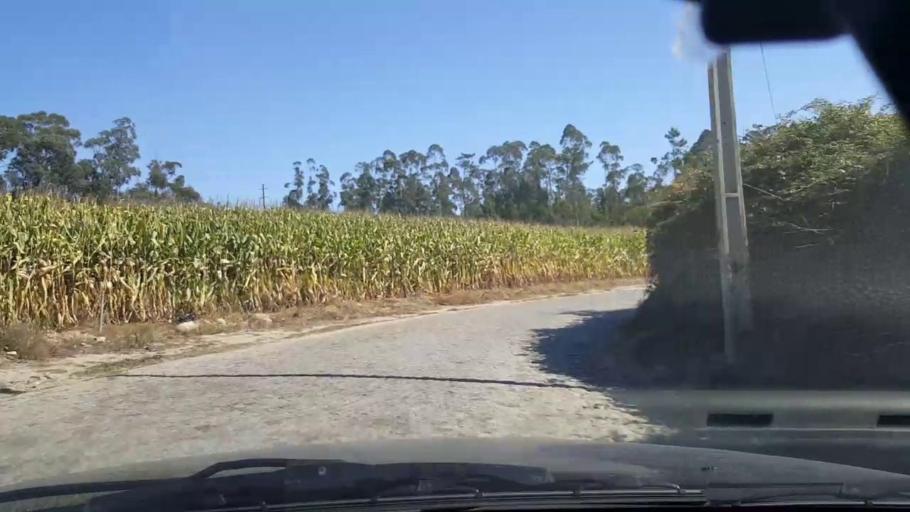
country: PT
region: Porto
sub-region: Vila do Conde
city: Arvore
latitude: 41.3167
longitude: -8.6900
